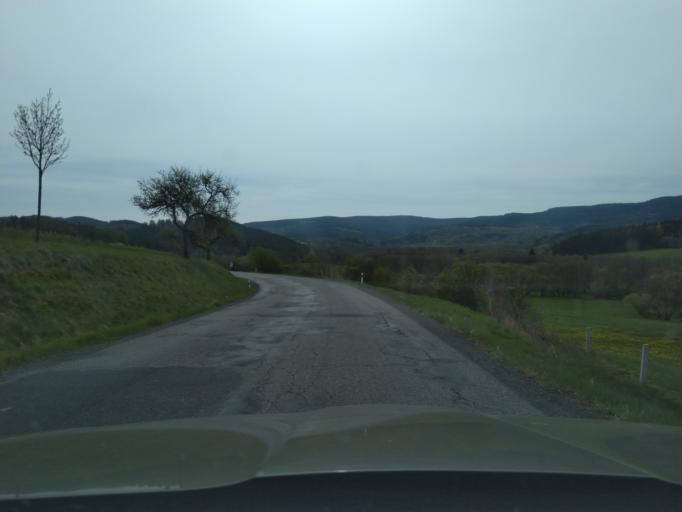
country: CZ
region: Plzensky
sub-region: Okres Klatovy
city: Kasperske Hory
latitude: 49.1975
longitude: 13.6162
